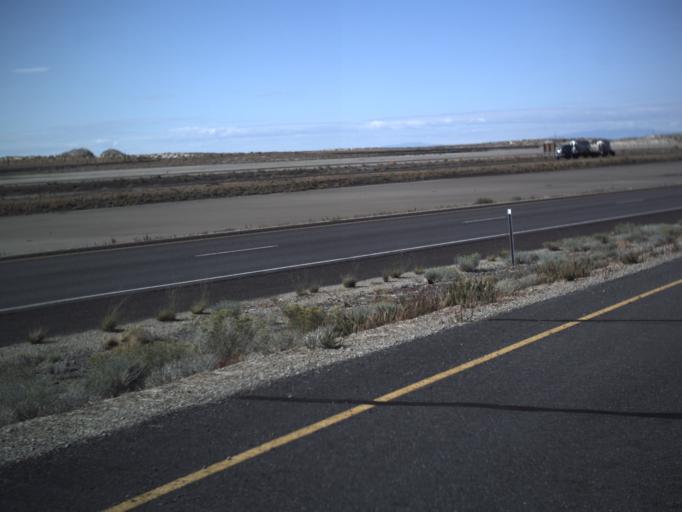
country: US
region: Utah
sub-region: Tooele County
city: Wendover
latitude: 40.7276
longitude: -113.2616
